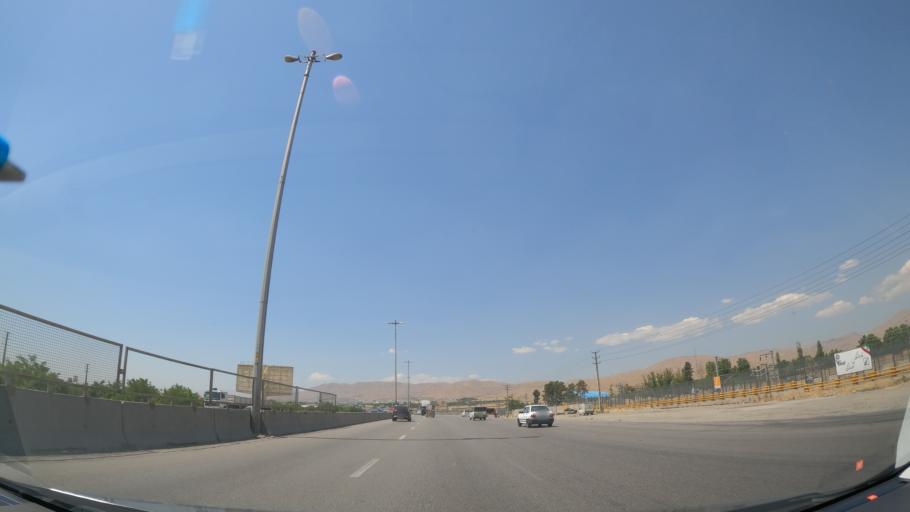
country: IR
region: Alborz
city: Karaj
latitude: 35.8529
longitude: 50.9089
